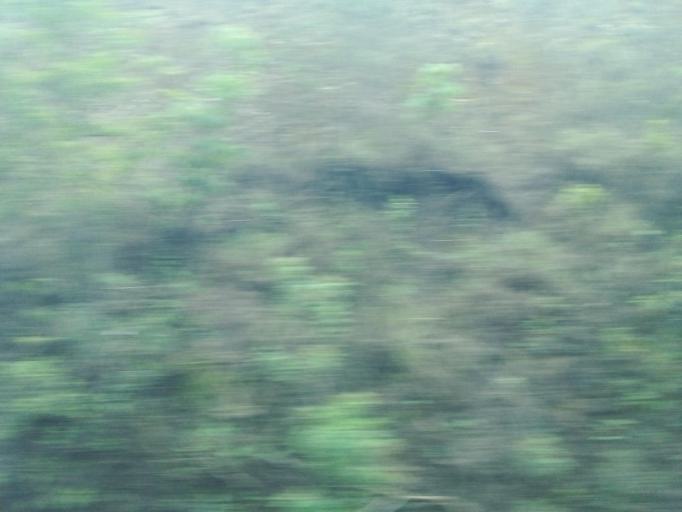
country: BR
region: Minas Gerais
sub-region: Rio Piracicaba
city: Rio Piracicaba
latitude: -19.9466
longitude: -43.1907
